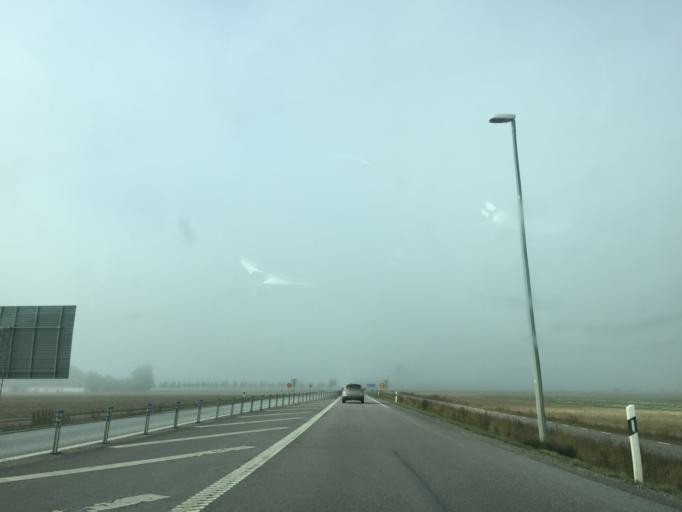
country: SE
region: Skane
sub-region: Lunds Kommun
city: Genarp
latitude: 55.6613
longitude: 13.3324
